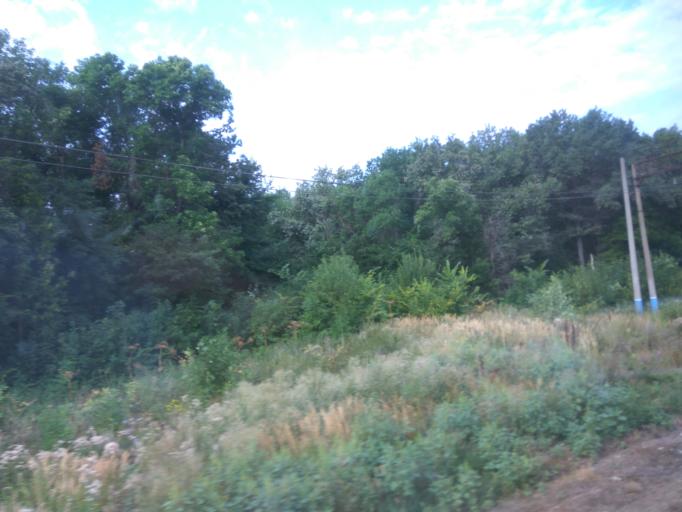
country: RU
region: Saratov
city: Rtishchevo
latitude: 52.2020
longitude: 43.8957
